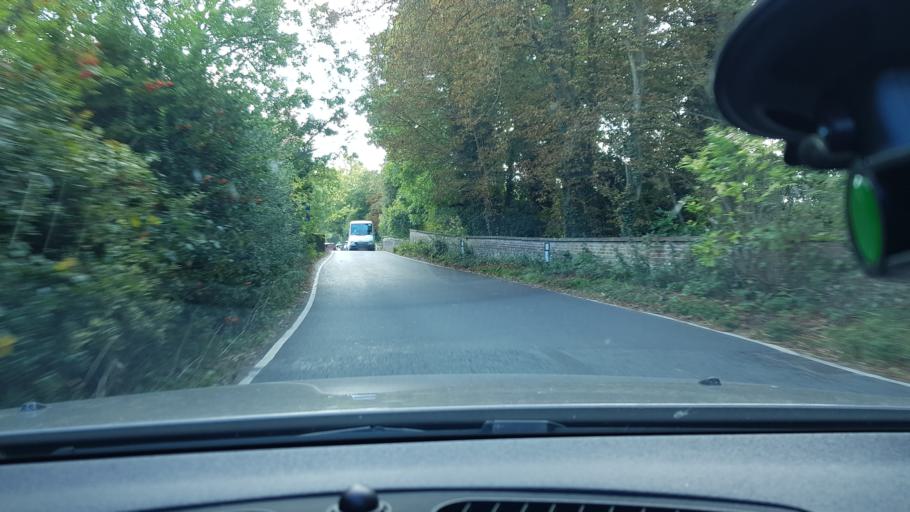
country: GB
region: England
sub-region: West Berkshire
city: Kintbury
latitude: 51.4060
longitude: -1.4457
